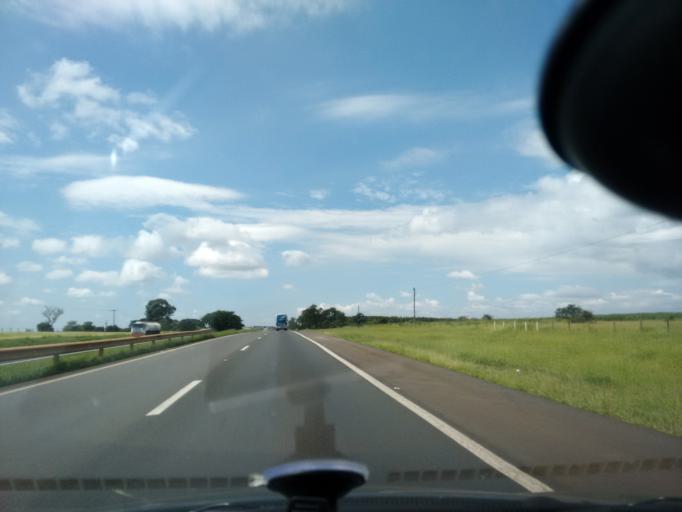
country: BR
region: Sao Paulo
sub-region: Ibate
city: Ibate
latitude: -21.9208
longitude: -48.0343
